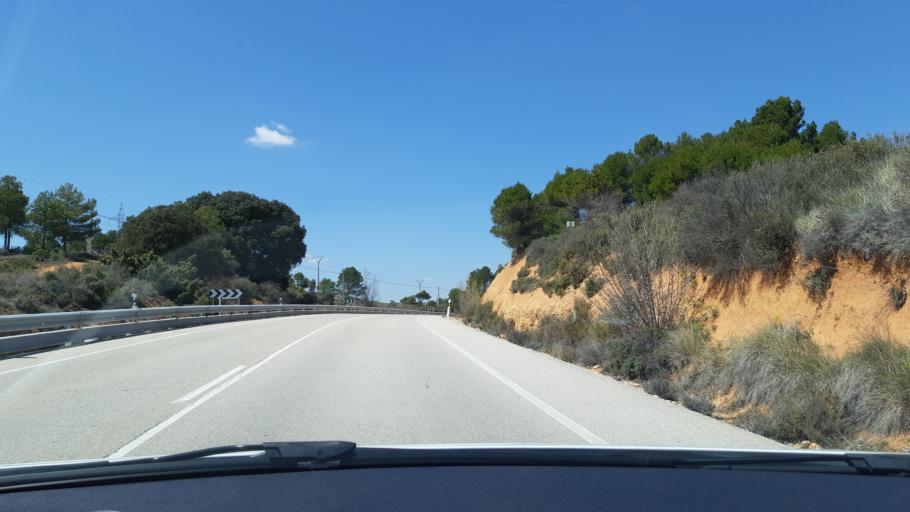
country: ES
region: Castille-La Mancha
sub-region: Provincia de Guadalajara
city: Cifuentes
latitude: 40.7990
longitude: -2.6609
